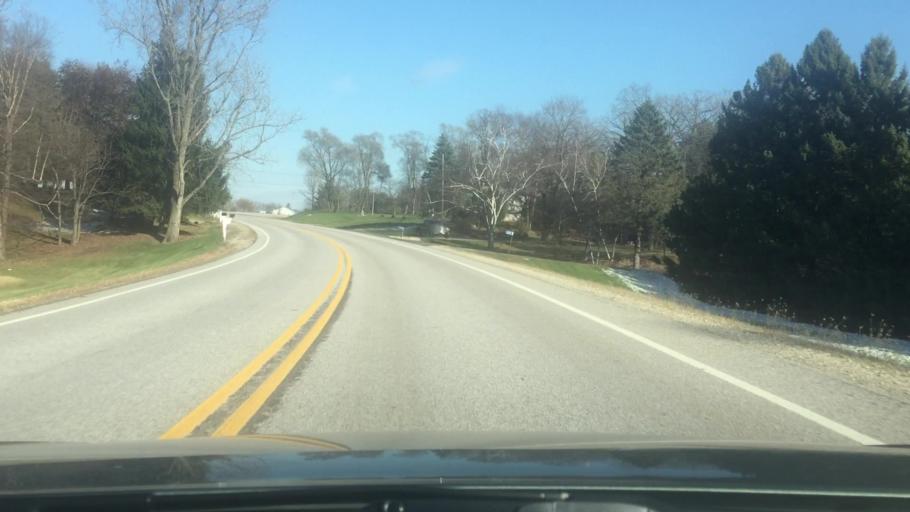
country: US
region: Wisconsin
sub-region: Jefferson County
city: Lake Koshkonong
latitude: 42.9478
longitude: -88.8877
